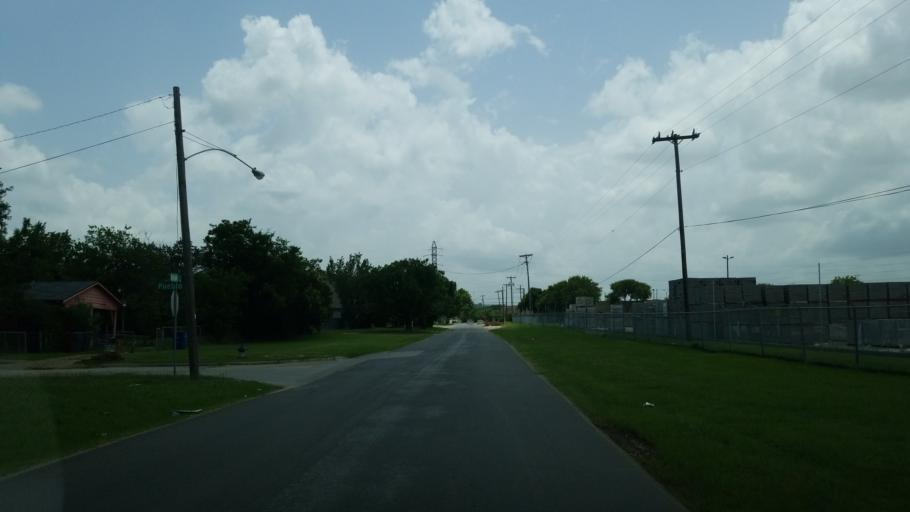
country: US
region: Texas
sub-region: Dallas County
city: Cockrell Hill
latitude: 32.7810
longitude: -96.8826
